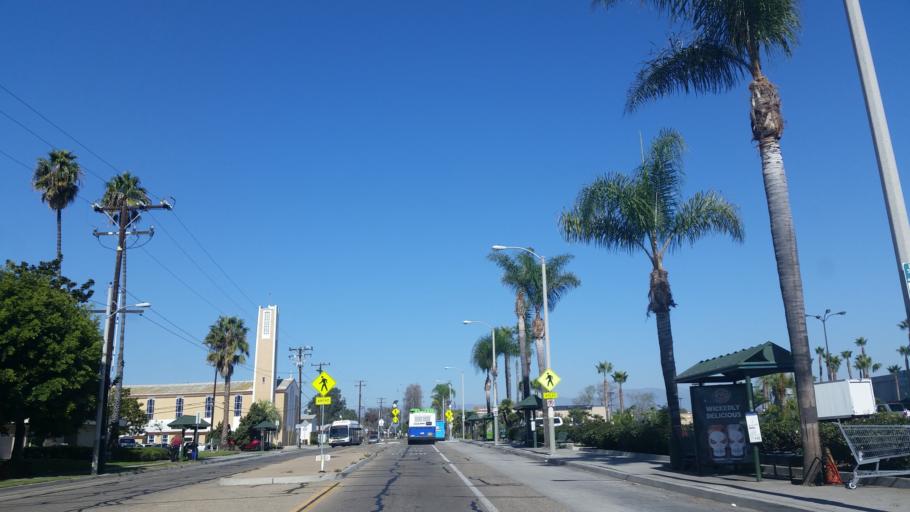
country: US
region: California
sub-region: Ventura County
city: Oxnard
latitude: 34.1750
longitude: -119.1811
